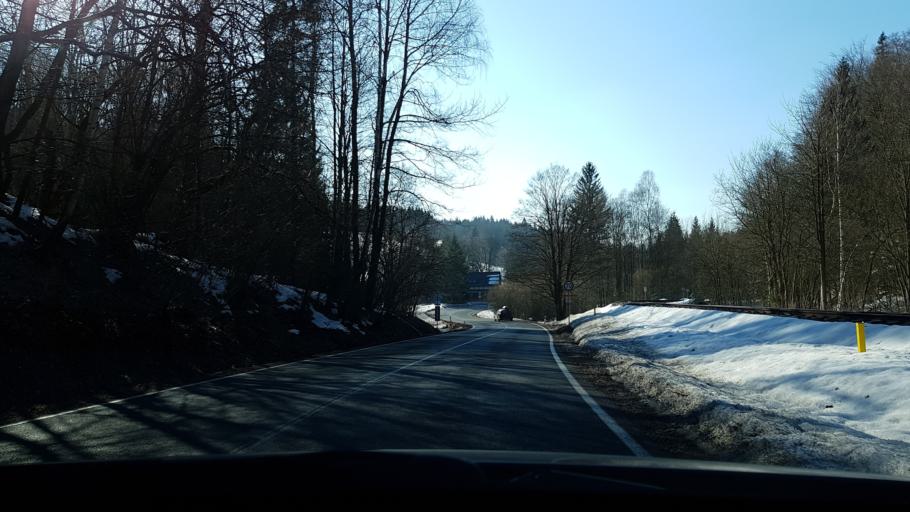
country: CZ
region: Olomoucky
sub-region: Okres Sumperk
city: Stare Mesto
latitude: 50.1358
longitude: 17.0126
